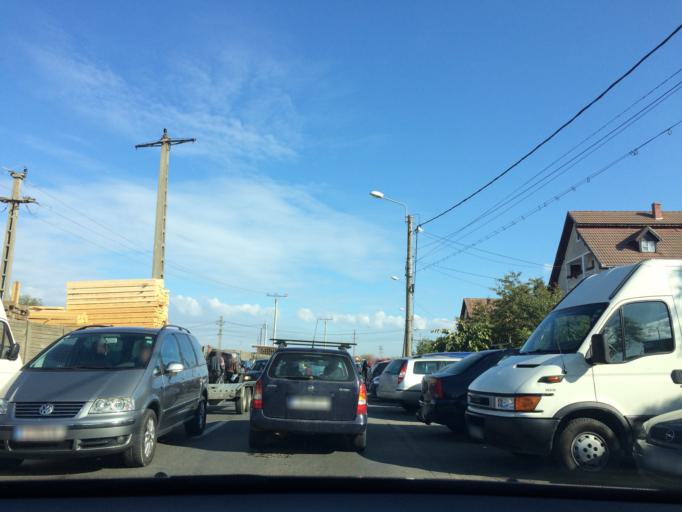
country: RO
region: Timis
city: Timisoara
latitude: 45.7692
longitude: 21.1960
